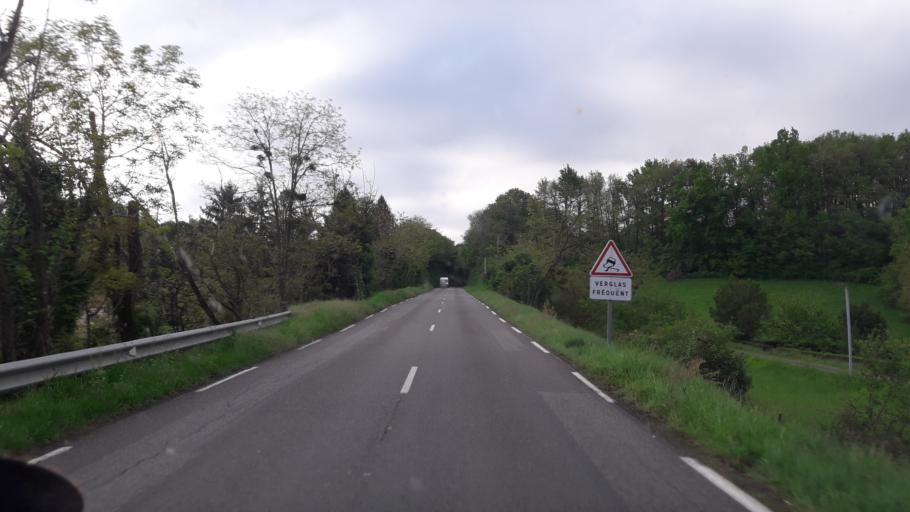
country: FR
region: Midi-Pyrenees
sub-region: Departement de la Haute-Garonne
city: Cazeres
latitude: 43.2015
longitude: 1.0935
